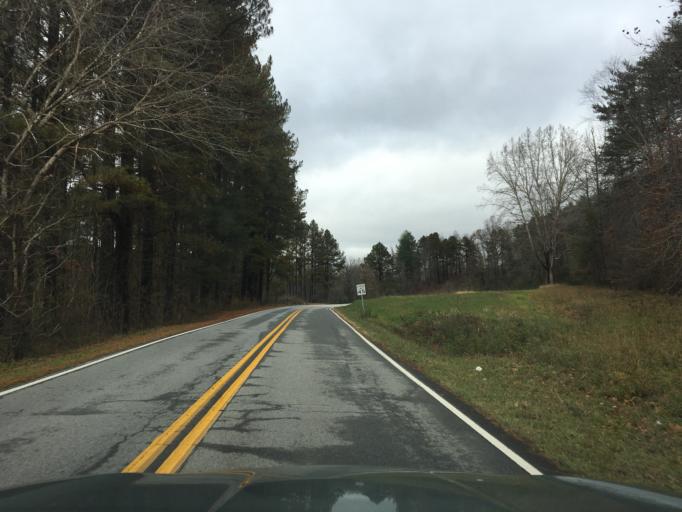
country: US
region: North Carolina
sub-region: Rutherford County
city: Rutherfordton
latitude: 35.3152
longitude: -81.9807
